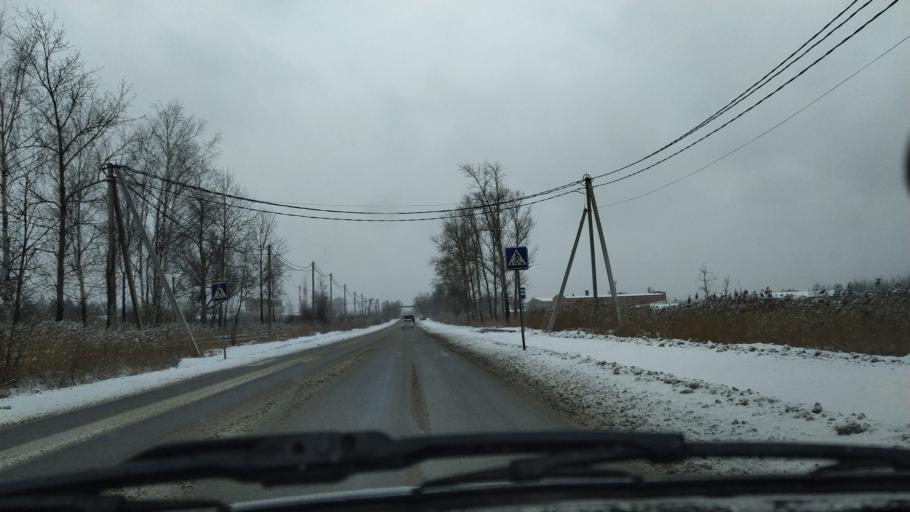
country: RU
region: Moskovskaya
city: Lopatinskiy
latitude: 55.3508
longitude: 38.7403
